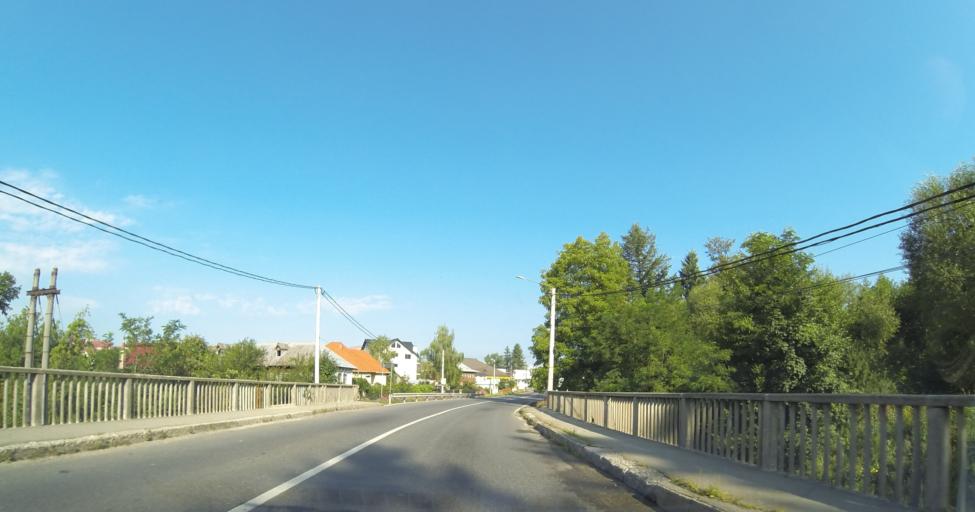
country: RO
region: Valcea
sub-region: Comuna Horezu
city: Horezu
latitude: 45.1449
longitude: 23.9958
